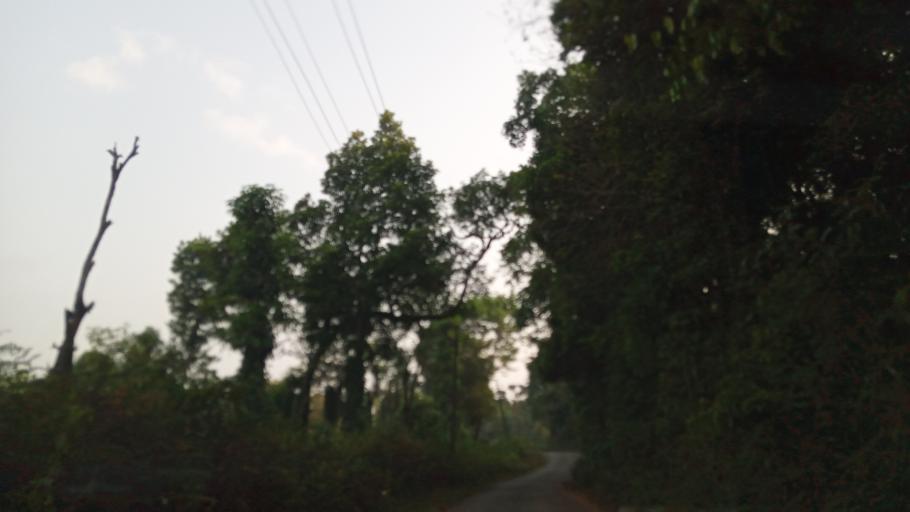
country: IN
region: Karnataka
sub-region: Chikmagalur
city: Mudigere
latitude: 13.0001
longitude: 75.6232
